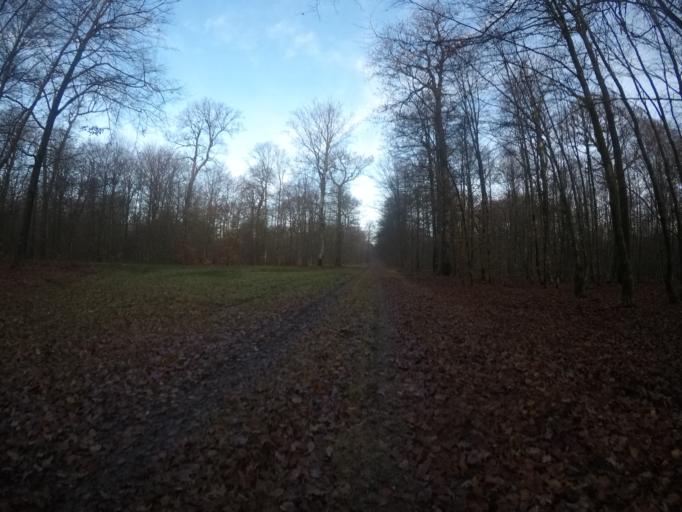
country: BE
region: Wallonia
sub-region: Province du Luxembourg
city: Habay-la-Vieille
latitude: 49.7540
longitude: 5.6700
